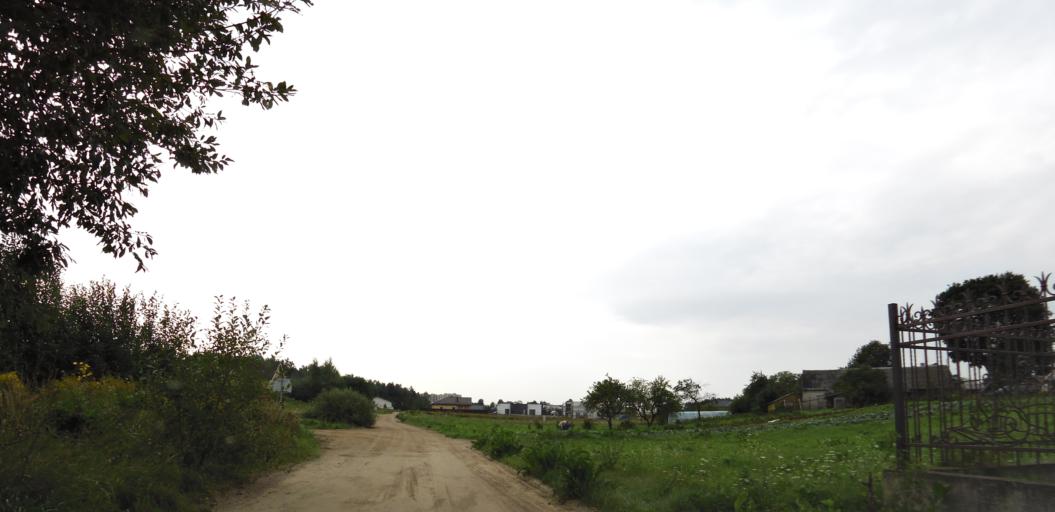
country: LT
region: Vilnius County
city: Pasilaiciai
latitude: 54.7558
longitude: 25.2297
